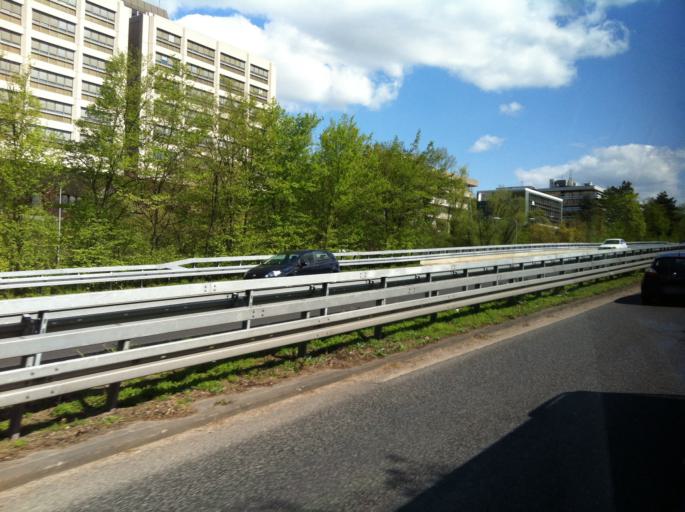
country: DE
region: Hesse
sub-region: Regierungsbezirk Darmstadt
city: Wiesbaden
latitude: 50.0686
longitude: 8.2623
